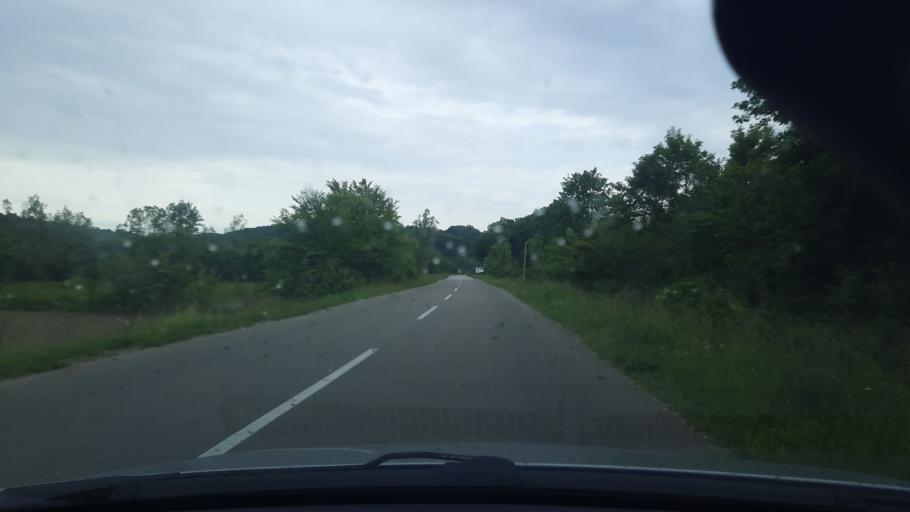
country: RS
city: Jarebice
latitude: 44.4866
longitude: 19.4839
